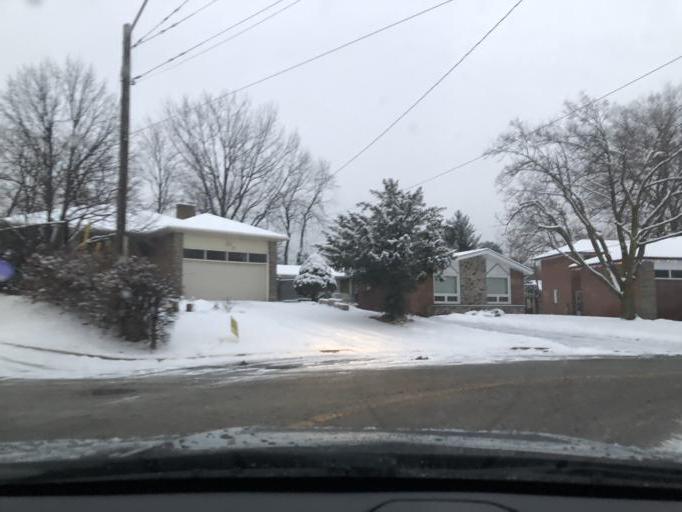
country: CA
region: Ontario
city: Toronto
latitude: 43.6977
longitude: -79.4786
